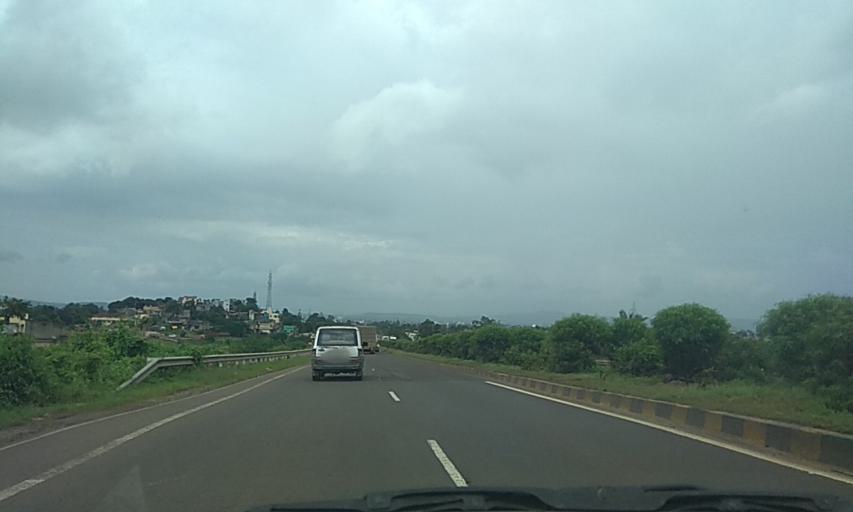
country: IN
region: Maharashtra
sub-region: Kolhapur
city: Kolhapur
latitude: 16.6779
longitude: 74.2708
